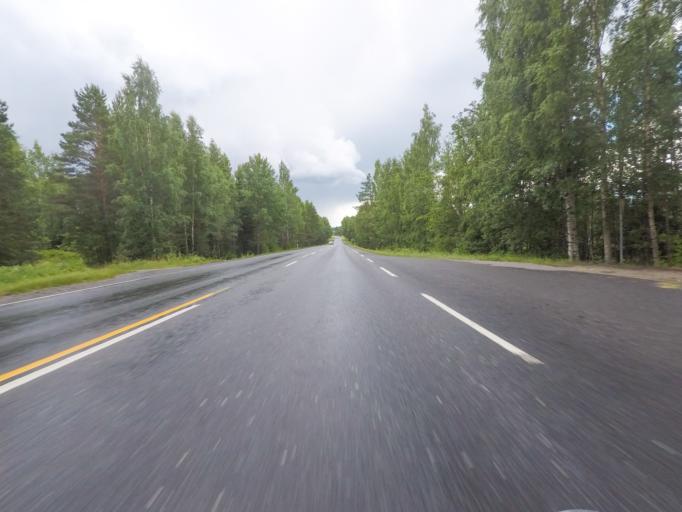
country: FI
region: Paijanne Tavastia
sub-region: Lahti
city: Hartola
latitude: 61.6330
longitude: 26.0152
